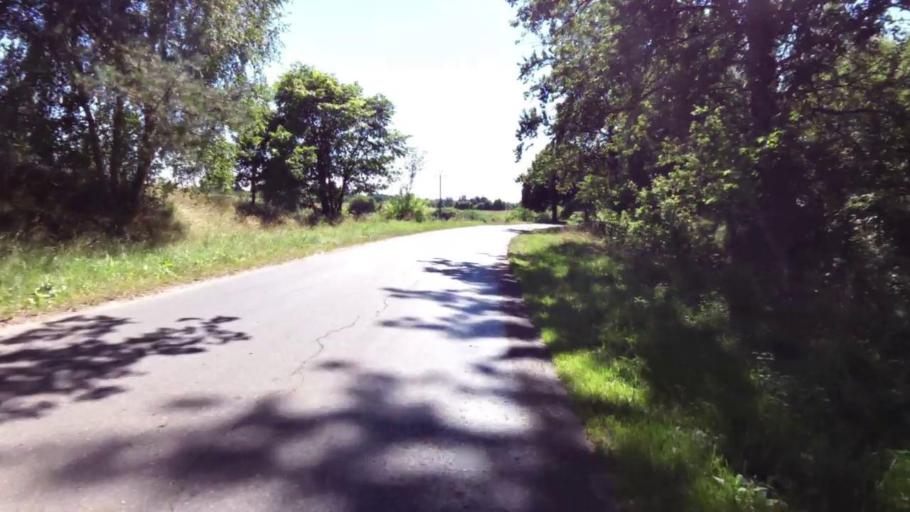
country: PL
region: West Pomeranian Voivodeship
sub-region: Powiat szczecinecki
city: Bialy Bor
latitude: 53.9291
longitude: 16.8520
